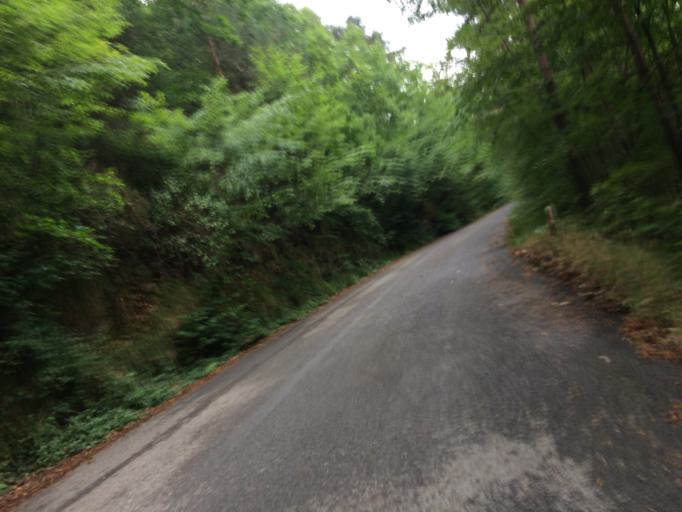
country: IT
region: Liguria
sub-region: Provincia di Imperia
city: Triora
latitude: 43.9735
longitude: 7.7447
